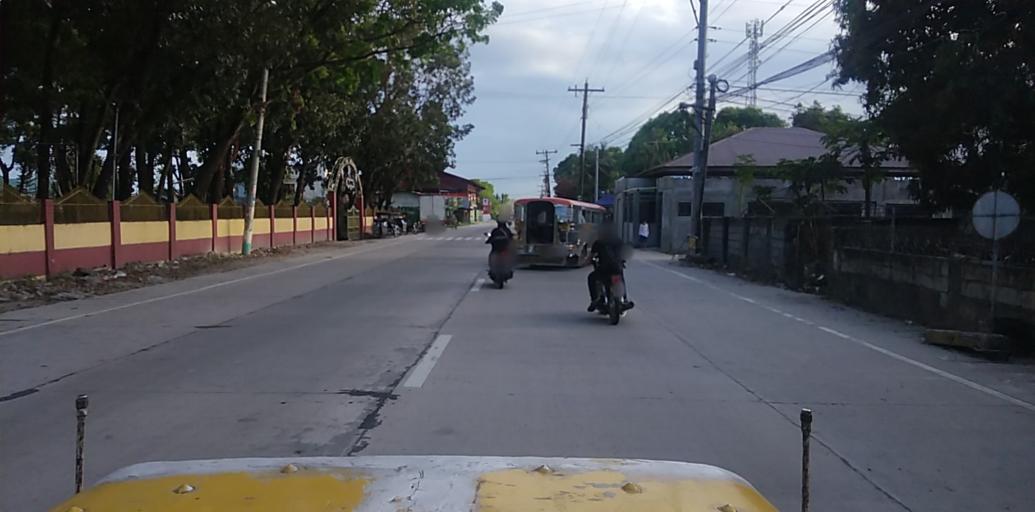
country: PH
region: Central Luzon
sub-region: Province of Pampanga
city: Anao
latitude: 15.1407
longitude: 120.6933
